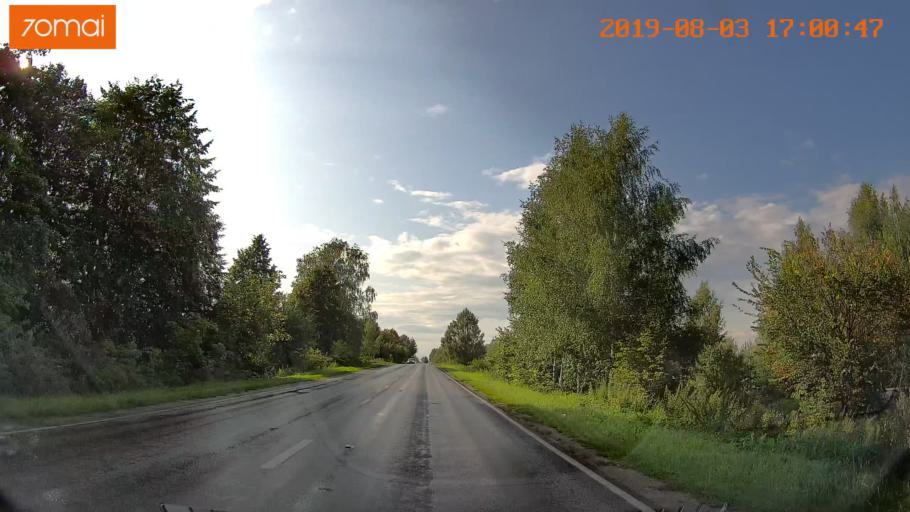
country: RU
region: Moskovskaya
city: Voskresensk
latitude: 55.3396
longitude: 38.6134
